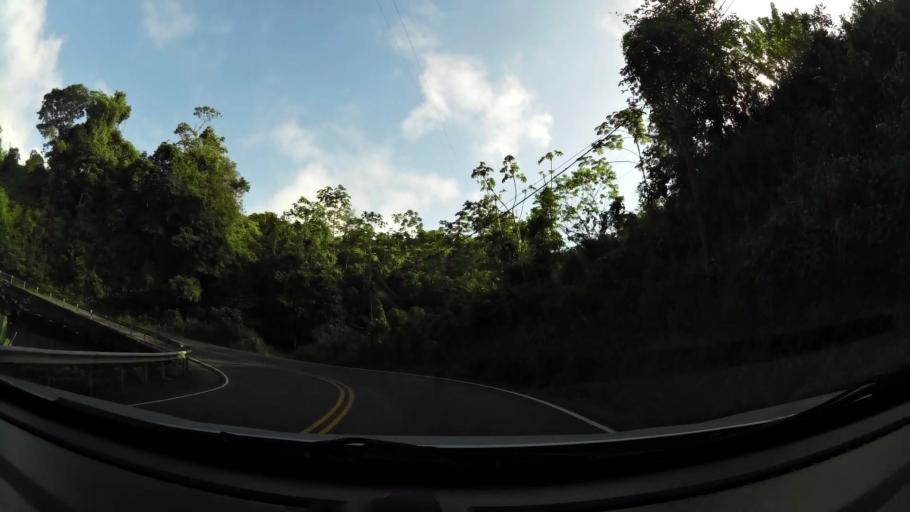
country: CR
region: Limon
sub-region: Canton de Siquirres
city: Siquirres
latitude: 10.0476
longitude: -83.5486
